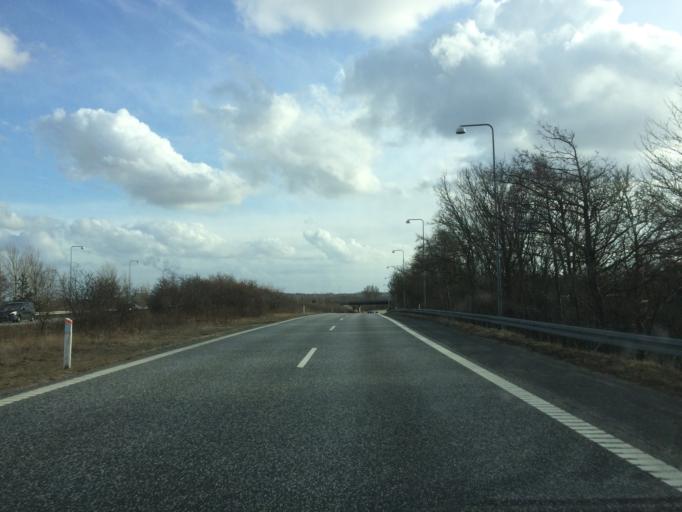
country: DK
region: North Denmark
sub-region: Alborg Kommune
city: Vestbjerg
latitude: 57.0880
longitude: 9.9678
